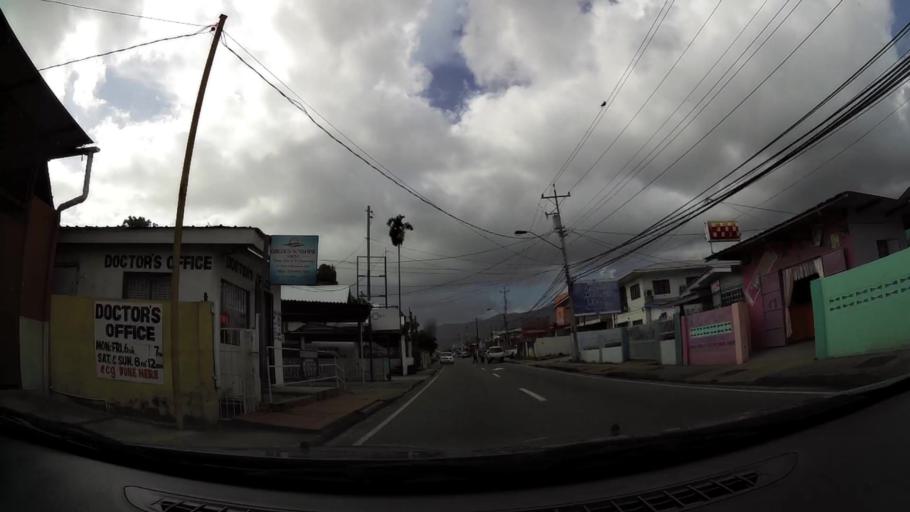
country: TT
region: Tunapuna/Piarco
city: Arouca
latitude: 10.6375
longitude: -61.3468
